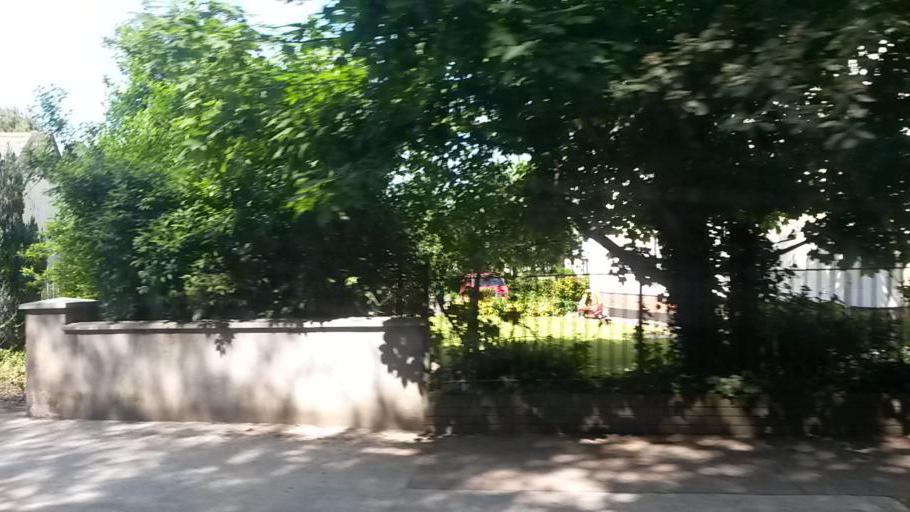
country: IE
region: Leinster
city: Donabate
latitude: 53.4872
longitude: -6.1587
